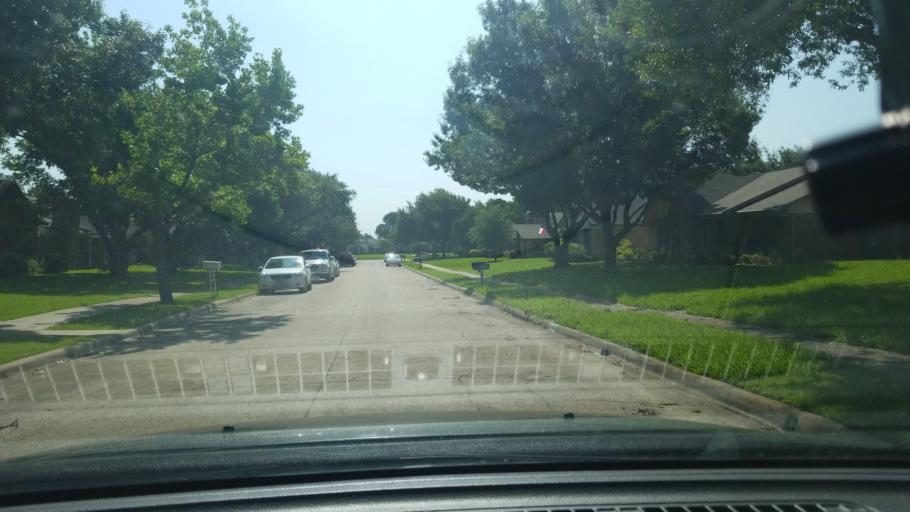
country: US
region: Texas
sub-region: Dallas County
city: Mesquite
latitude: 32.8182
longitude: -96.6199
